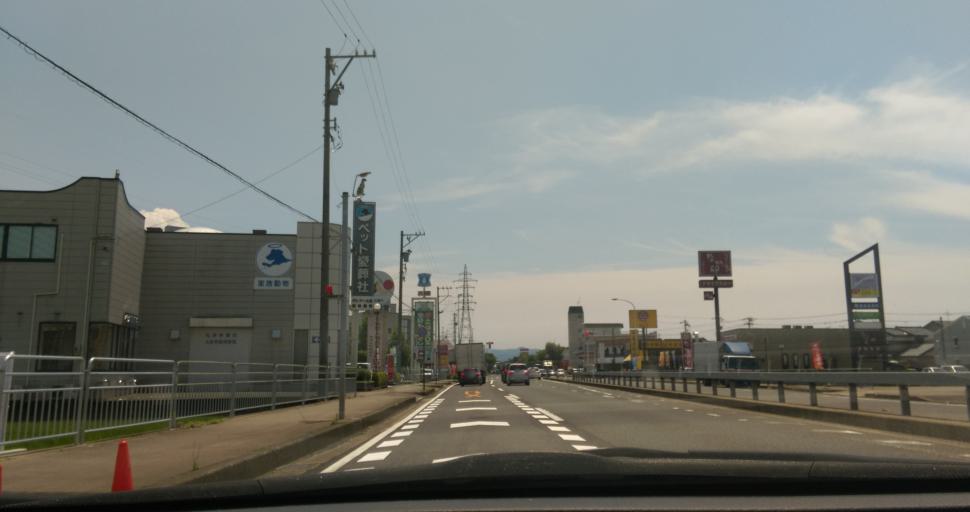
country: JP
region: Fukui
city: Sabae
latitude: 35.9406
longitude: 136.1925
